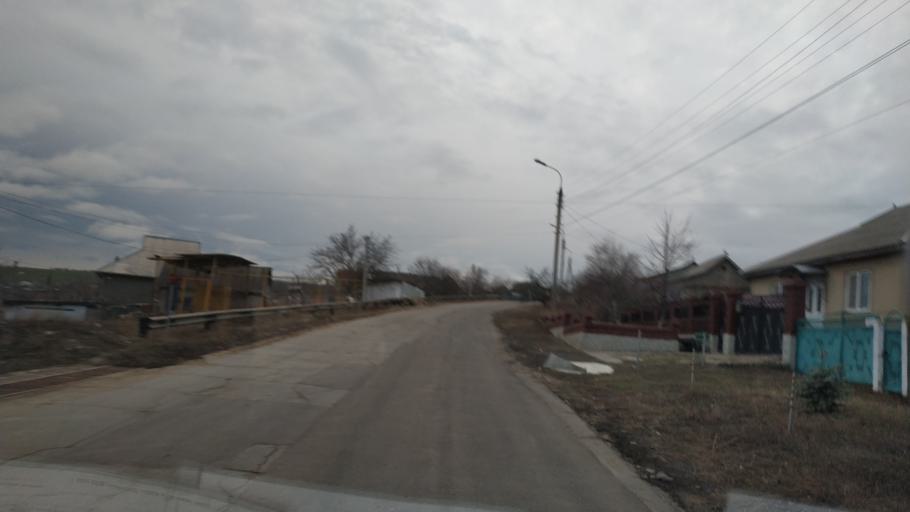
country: MD
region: Causeni
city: Causeni
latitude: 46.6278
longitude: 29.4020
